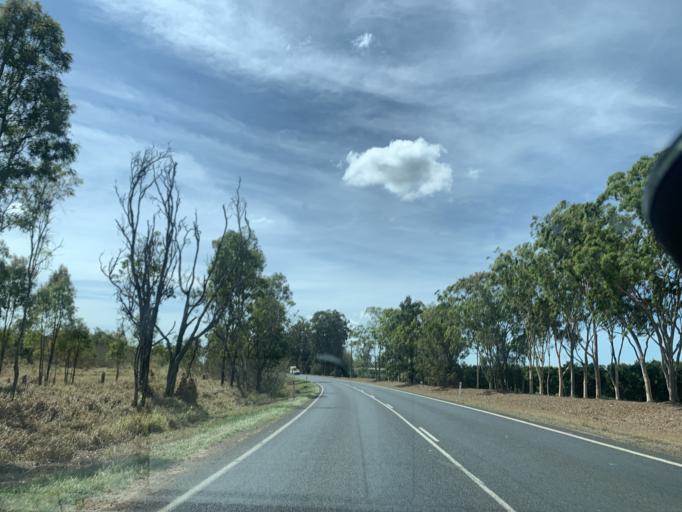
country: AU
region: Queensland
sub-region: Tablelands
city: Tolga
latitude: -17.1855
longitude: 145.4658
